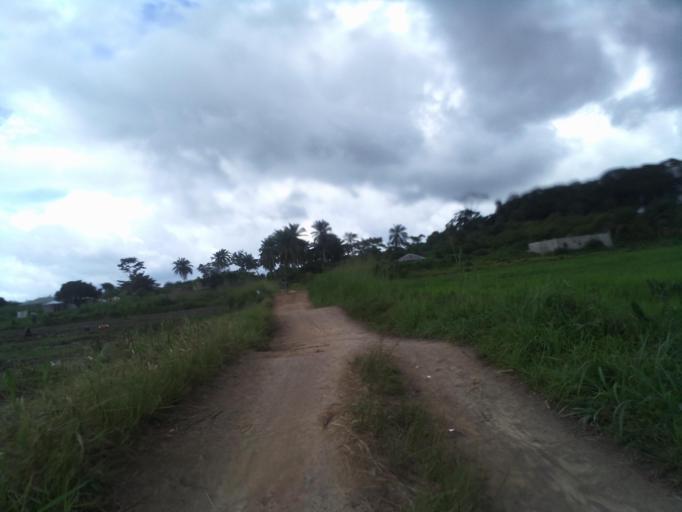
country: SL
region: Eastern Province
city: Kenema
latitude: 7.8359
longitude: -11.1859
